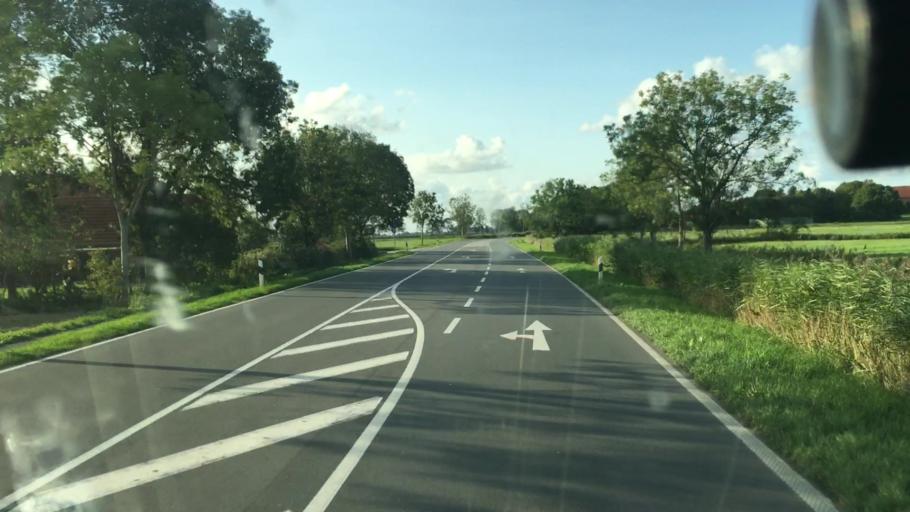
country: DE
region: Lower Saxony
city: Jever
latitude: 53.5924
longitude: 7.8714
